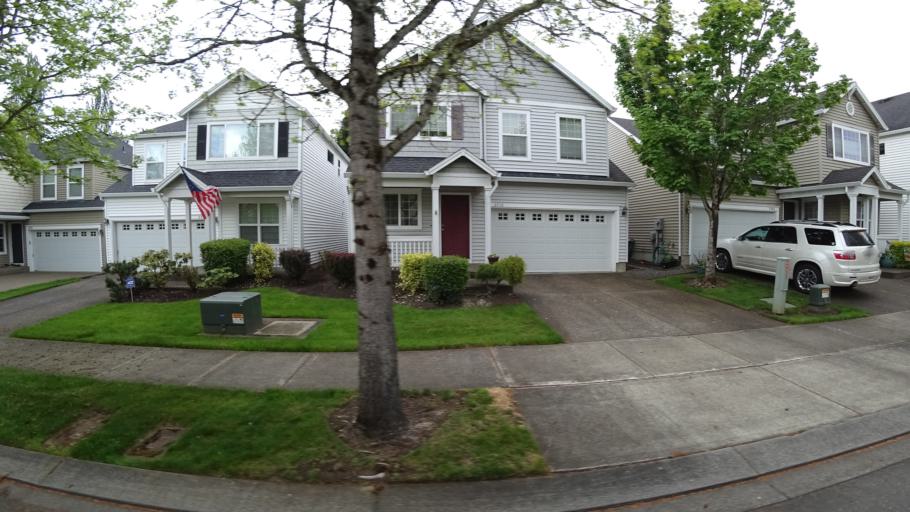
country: US
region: Oregon
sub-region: Washington County
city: Hillsboro
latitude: 45.5459
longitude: -122.9680
